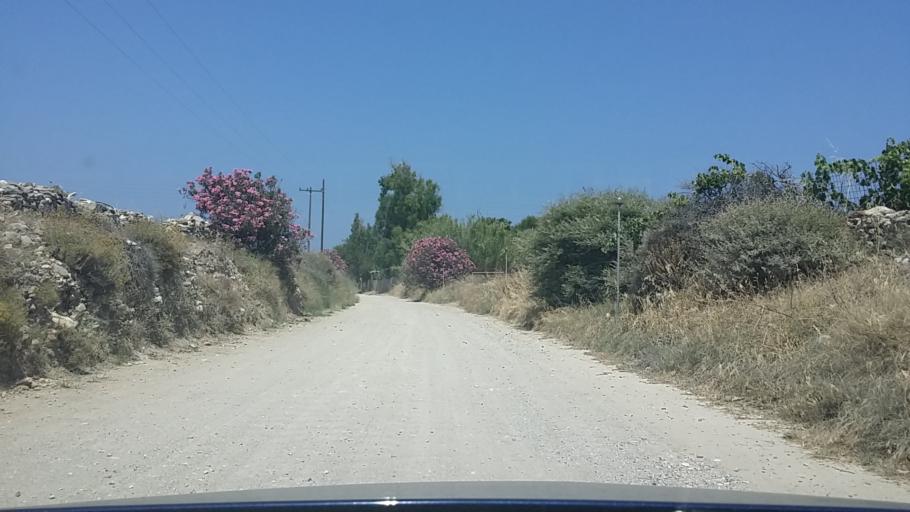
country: GR
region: South Aegean
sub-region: Nomos Kykladon
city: Paros
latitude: 37.0684
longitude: 25.1315
